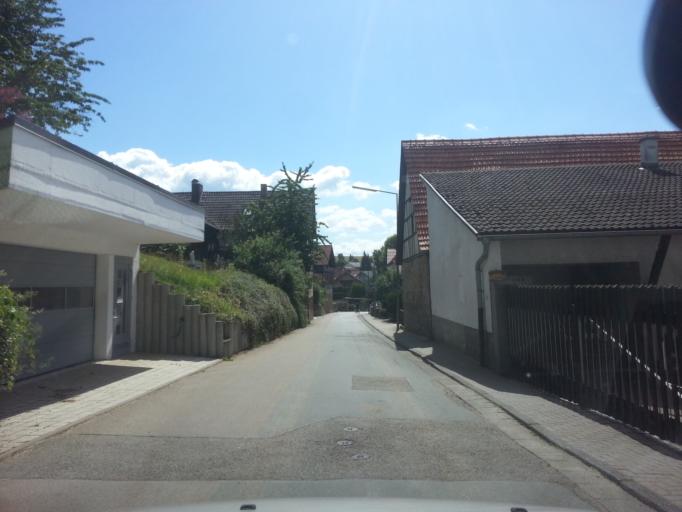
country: DE
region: Hesse
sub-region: Regierungsbezirk Darmstadt
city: Birkenau
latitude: 49.5855
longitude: 8.6980
